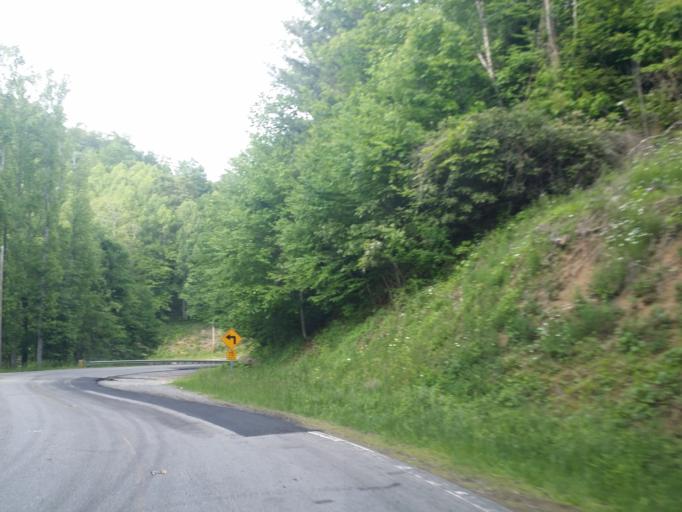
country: US
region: North Carolina
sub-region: Madison County
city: Marshall
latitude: 35.7200
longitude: -82.8399
